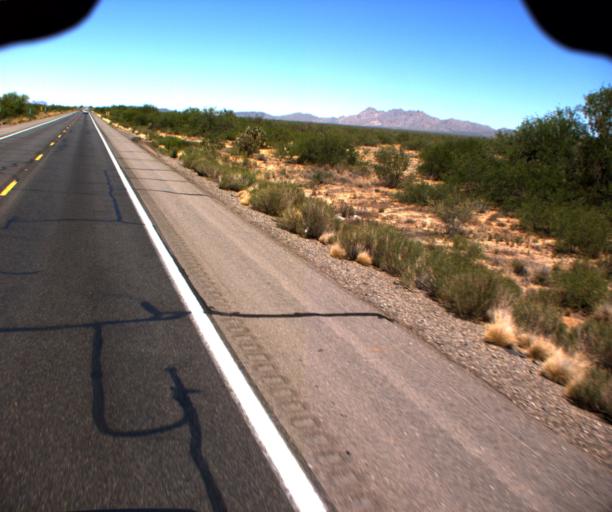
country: US
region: Arizona
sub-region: Yavapai County
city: Congress
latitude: 34.1123
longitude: -112.9345
